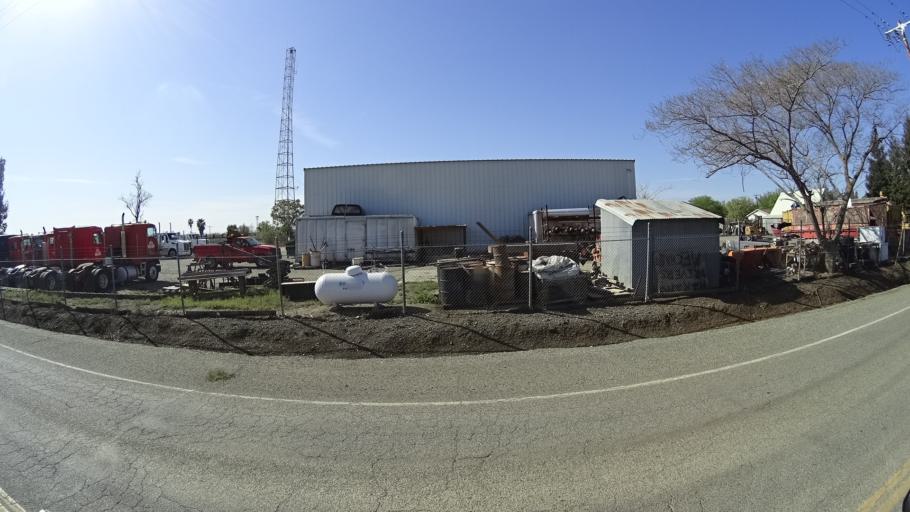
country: US
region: California
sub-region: Glenn County
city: Willows
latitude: 39.5388
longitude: -122.1942
